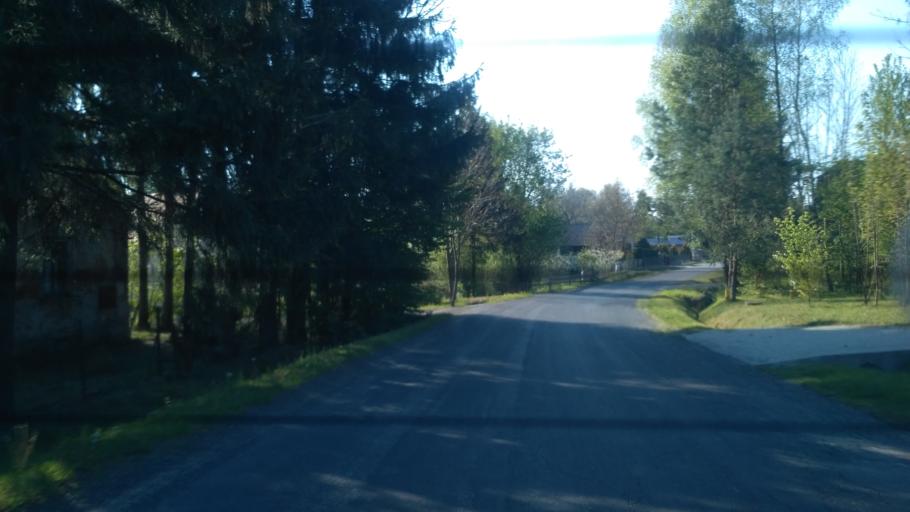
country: PL
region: Subcarpathian Voivodeship
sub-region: Powiat jaroslawski
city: Pruchnik
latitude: 49.8917
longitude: 22.5580
